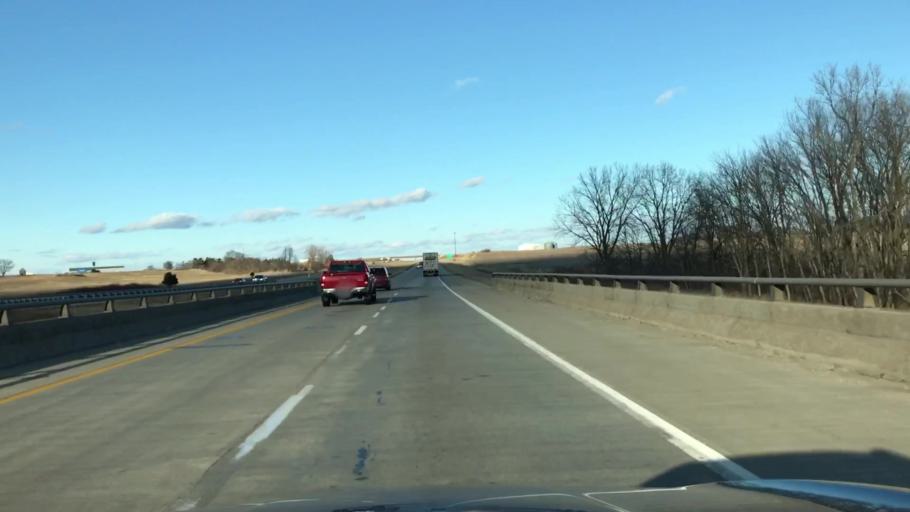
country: US
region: Illinois
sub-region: McLean County
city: Lexington
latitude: 40.6354
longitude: -88.8140
